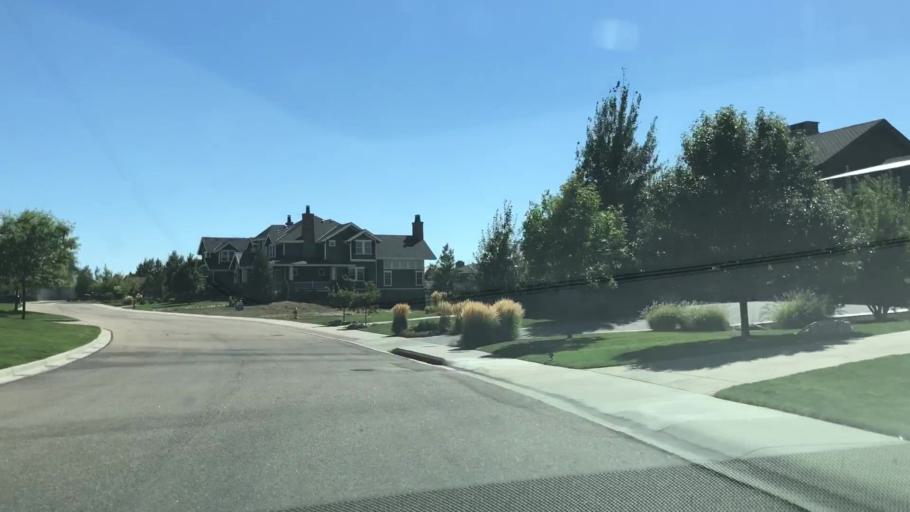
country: US
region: Colorado
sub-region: Weld County
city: Windsor
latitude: 40.5360
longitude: -104.9589
